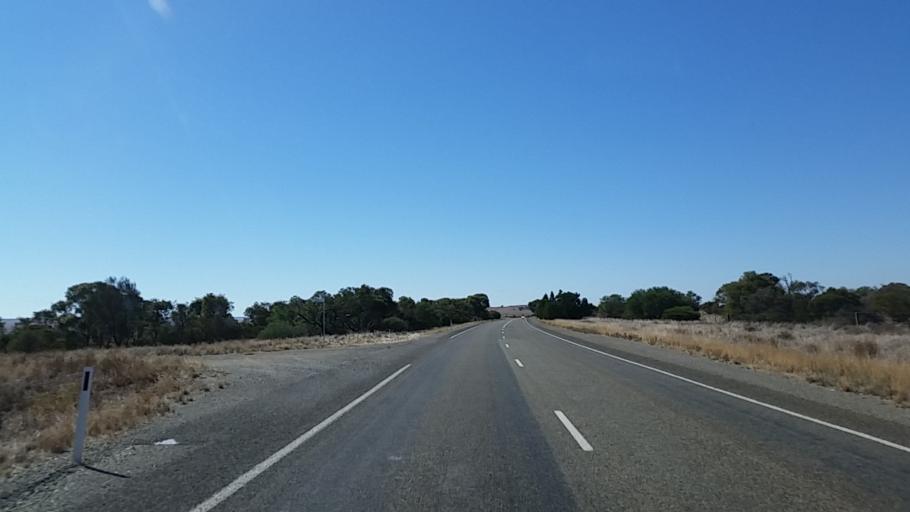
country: AU
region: South Australia
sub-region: Northern Areas
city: Jamestown
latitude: -33.2436
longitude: 138.8745
